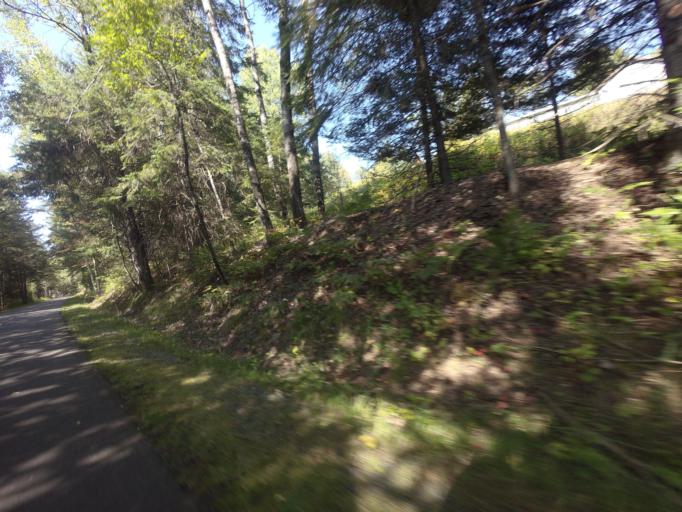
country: CA
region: Quebec
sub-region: Laurentides
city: Mont-Tremblant
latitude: 46.1274
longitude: -74.5728
